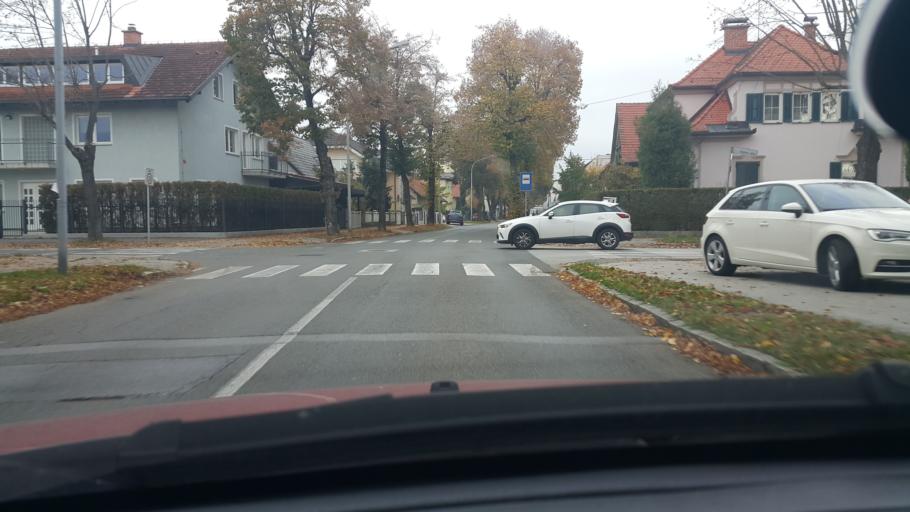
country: SI
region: Maribor
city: Maribor
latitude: 46.5463
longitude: 15.6392
